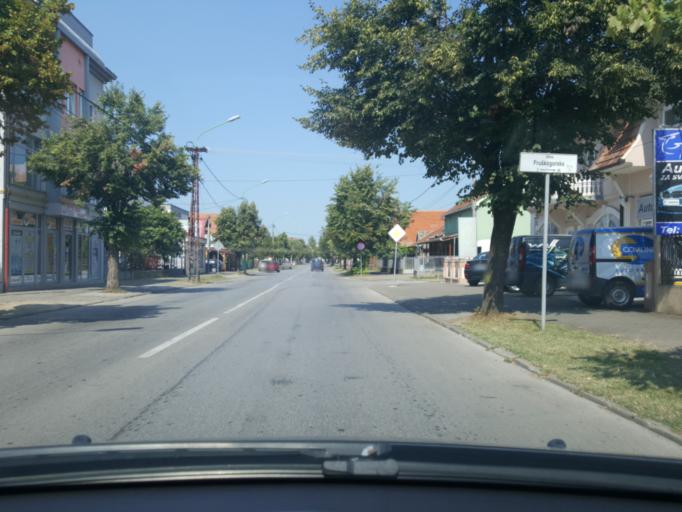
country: RS
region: Central Serbia
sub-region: Macvanski Okrug
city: Sabac
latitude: 44.7444
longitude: 19.6984
